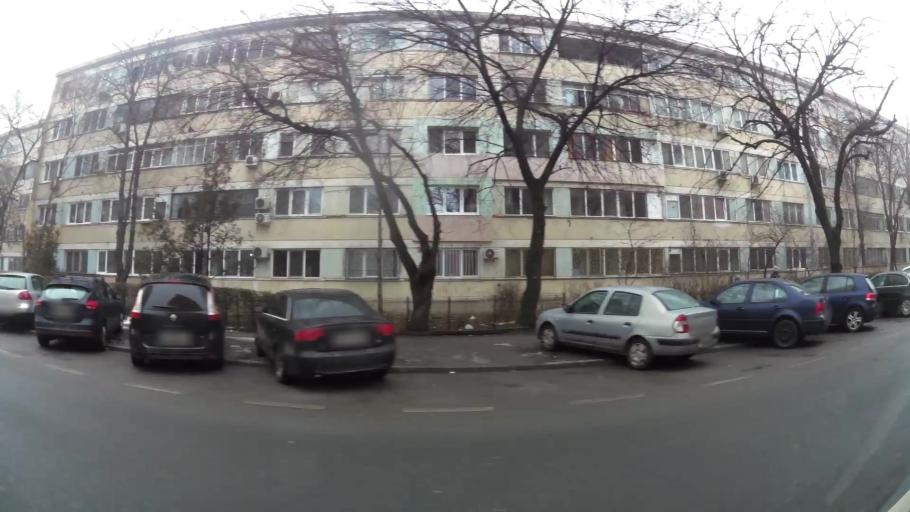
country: RO
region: Ilfov
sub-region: Comuna Chiajna
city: Rosu
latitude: 44.4555
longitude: 26.0437
